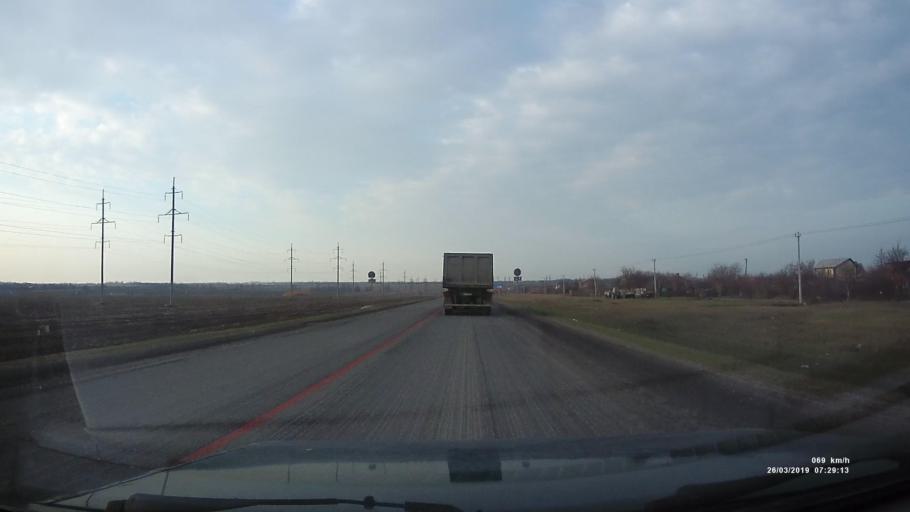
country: RU
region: Rostov
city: Novobessergenovka
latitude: 47.2472
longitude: 38.8184
